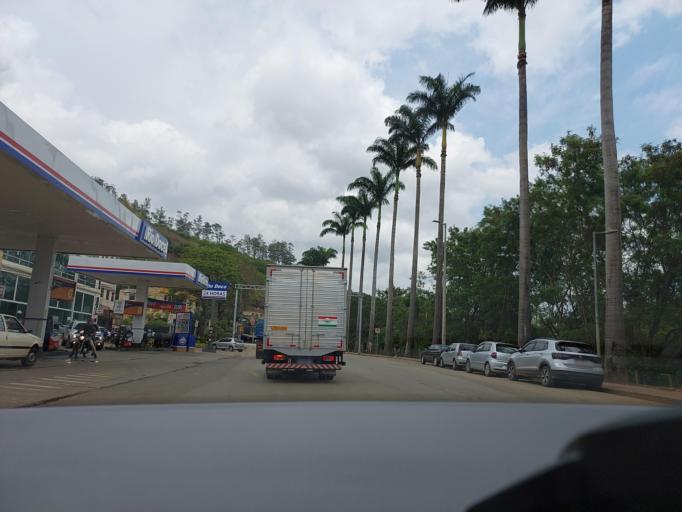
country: BR
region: Minas Gerais
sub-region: Ponte Nova
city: Ponte Nova
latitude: -20.4147
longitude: -42.9012
